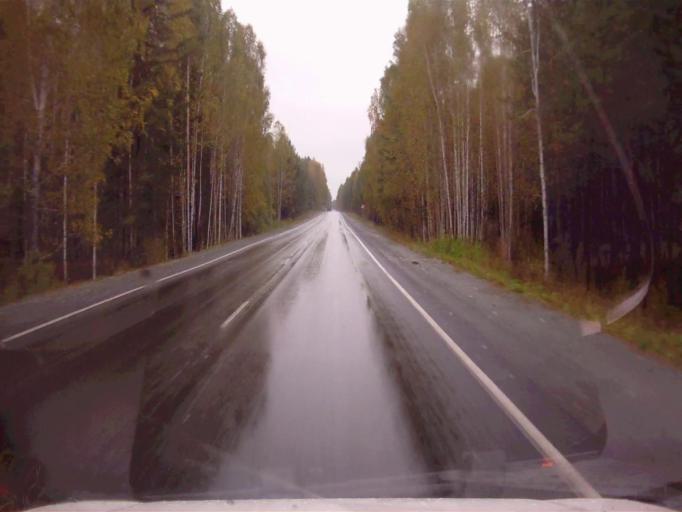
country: RU
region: Chelyabinsk
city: Tayginka
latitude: 55.5814
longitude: 60.6400
